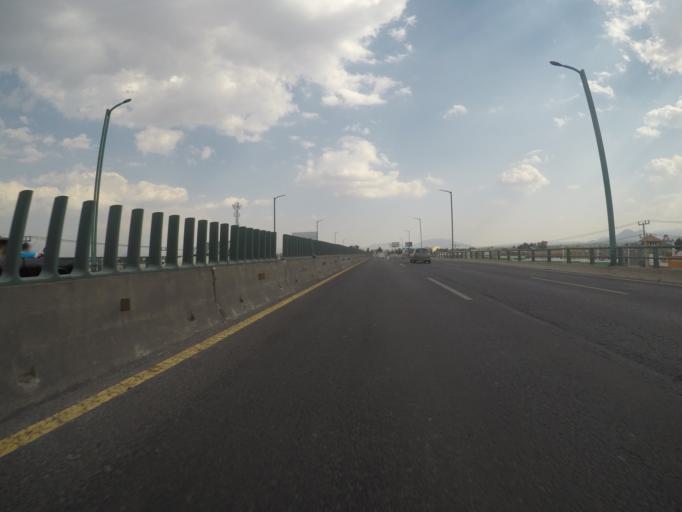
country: MX
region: Morelos
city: San Miguel Totocuitlapilco
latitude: 19.2358
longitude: -99.5980
